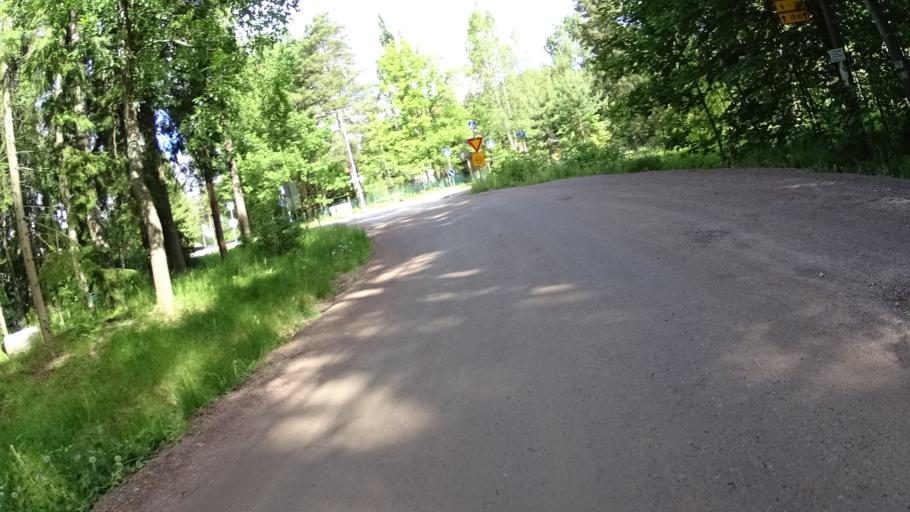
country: FI
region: Uusimaa
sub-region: Helsinki
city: Kilo
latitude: 60.1960
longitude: 24.8002
